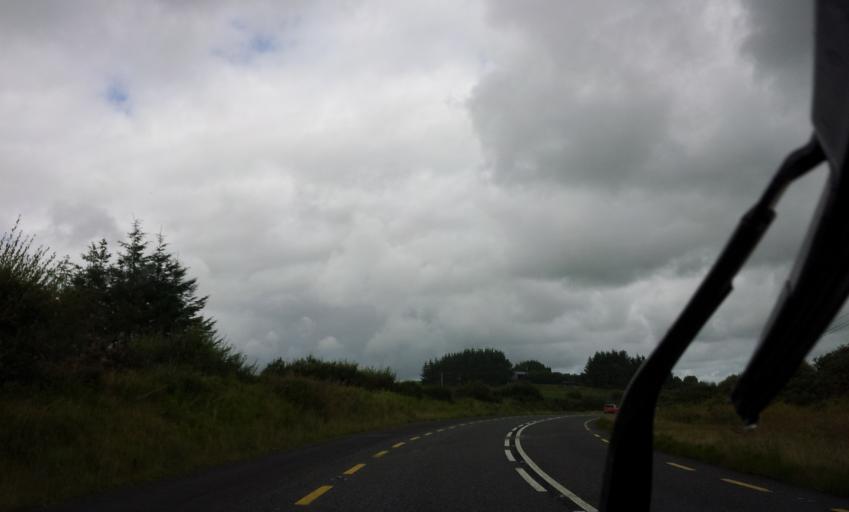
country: IE
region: Munster
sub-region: An Clar
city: Ennis
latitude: 52.8831
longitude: -9.1903
